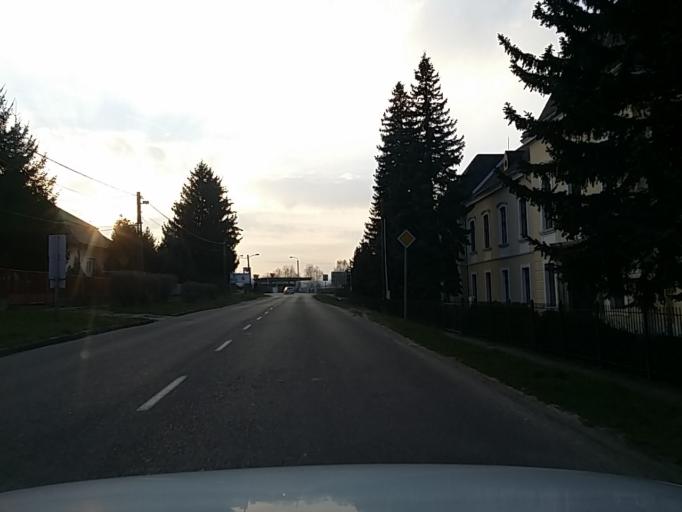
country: HU
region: Heves
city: Petervasara
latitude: 48.0190
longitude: 20.0977
